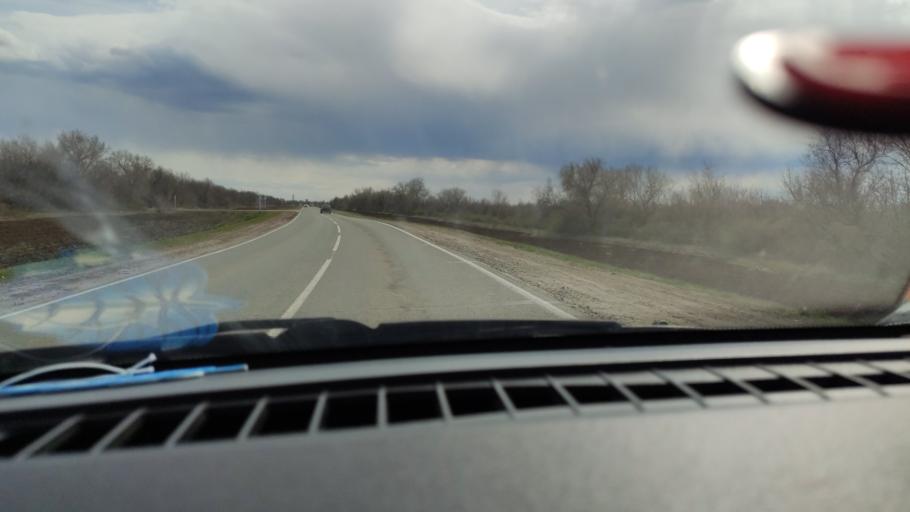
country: RU
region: Saratov
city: Privolzhskiy
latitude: 51.3381
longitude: 46.0404
